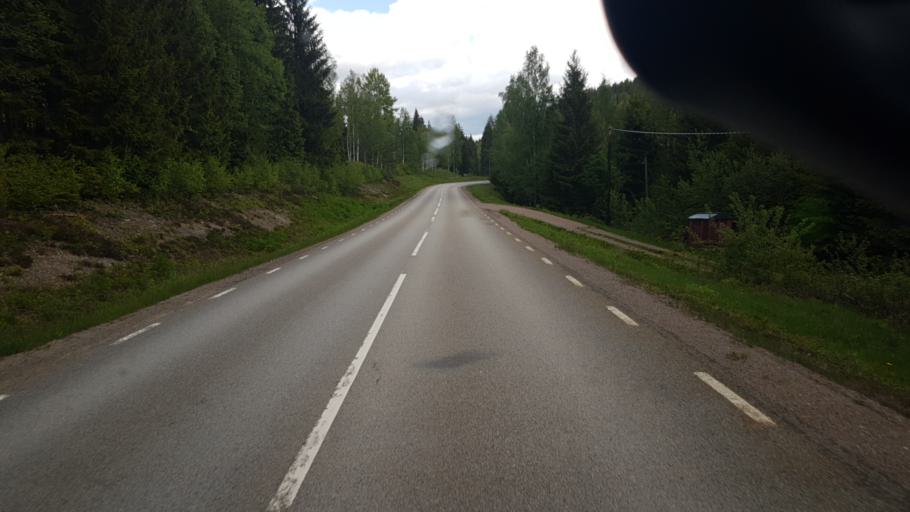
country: SE
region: Vaermland
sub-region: Arjangs Kommun
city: Arjaeng
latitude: 59.5601
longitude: 12.1738
